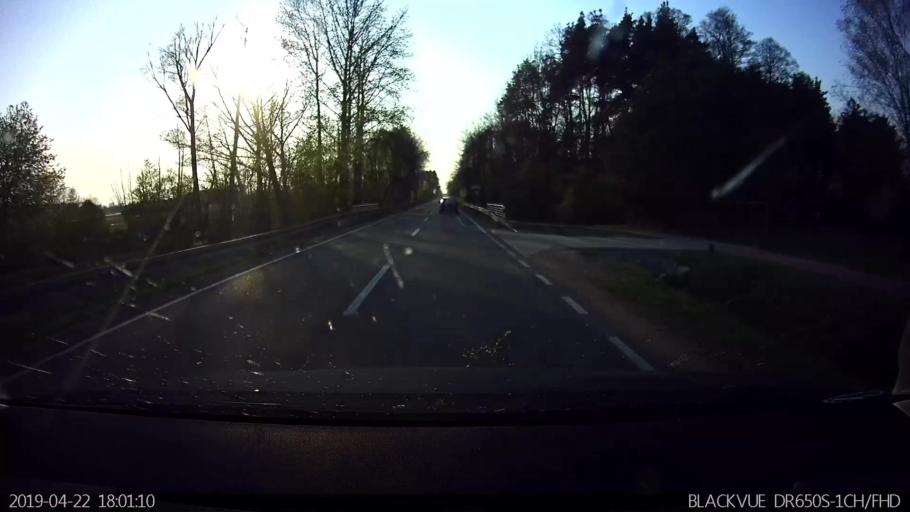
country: PL
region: Masovian Voivodeship
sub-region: Powiat wegrowski
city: Korytnica
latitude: 52.4779
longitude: 21.8344
